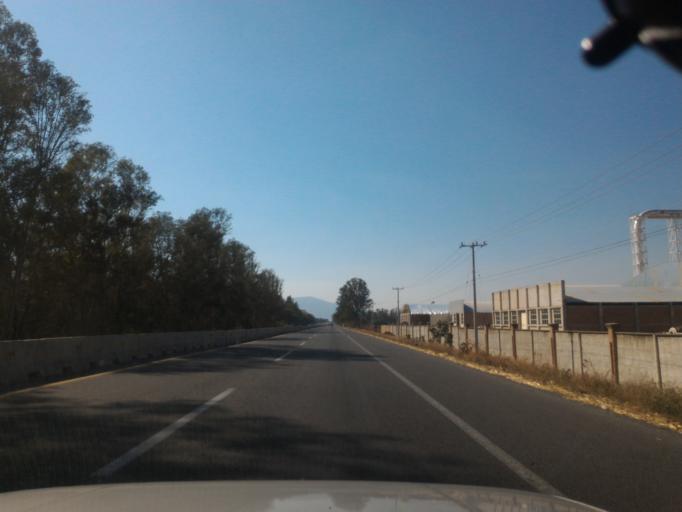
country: MX
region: Jalisco
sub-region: Poncitlan
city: Santa Cruz el Grande
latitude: 20.3655
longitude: -102.8469
